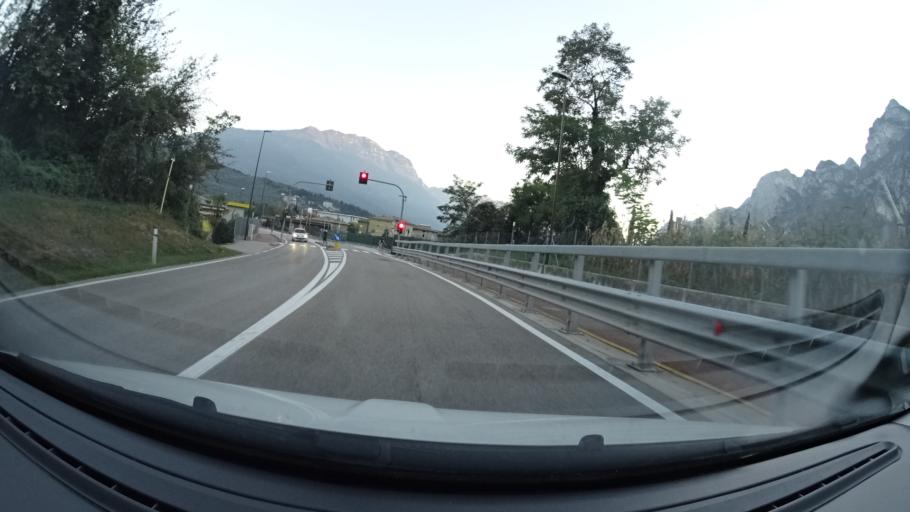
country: IT
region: Trentino-Alto Adige
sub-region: Provincia di Trento
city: Riva del Garda
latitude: 45.8884
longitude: 10.8548
